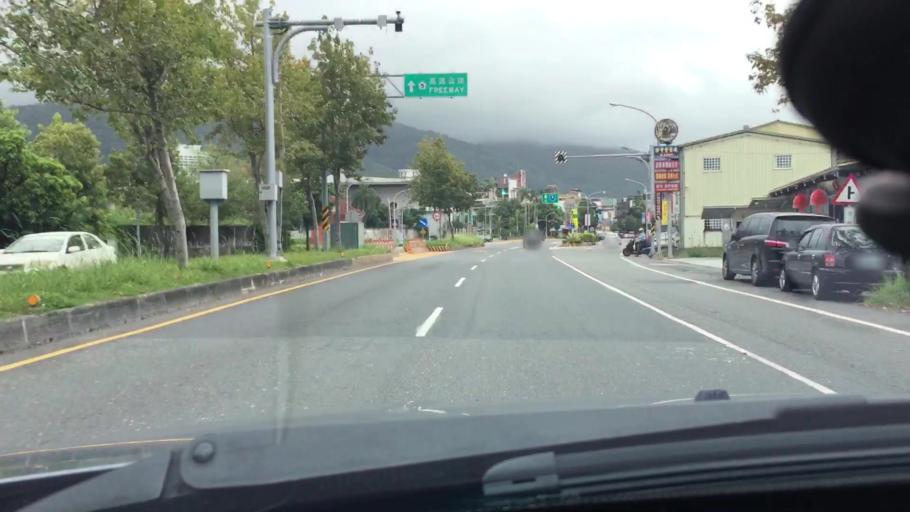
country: TW
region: Taiwan
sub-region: Yilan
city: Yilan
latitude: 24.8148
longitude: 121.7677
